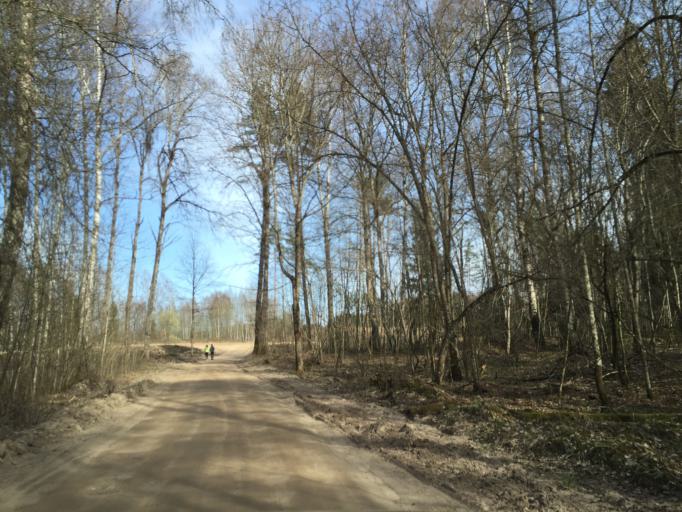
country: LV
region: Ikskile
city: Ikskile
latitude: 56.8432
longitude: 24.5387
